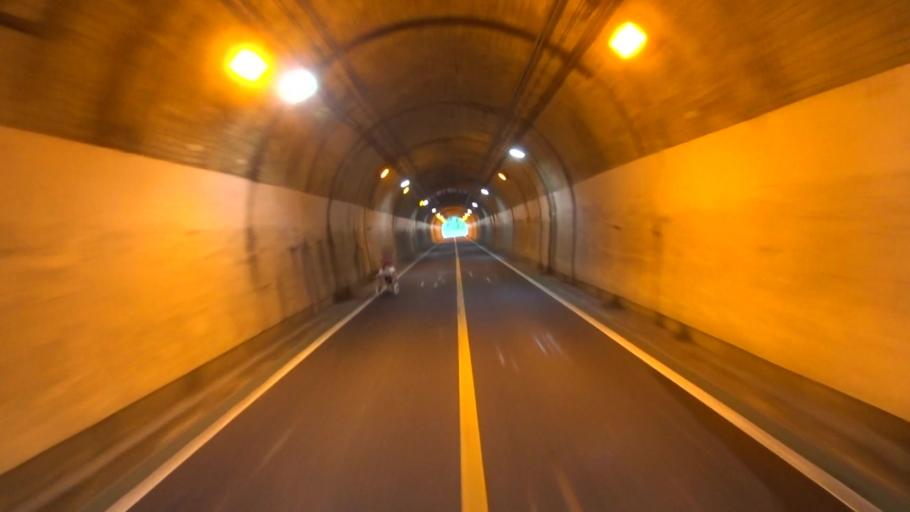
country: JP
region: Kyoto
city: Miyazu
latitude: 35.7351
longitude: 135.0934
